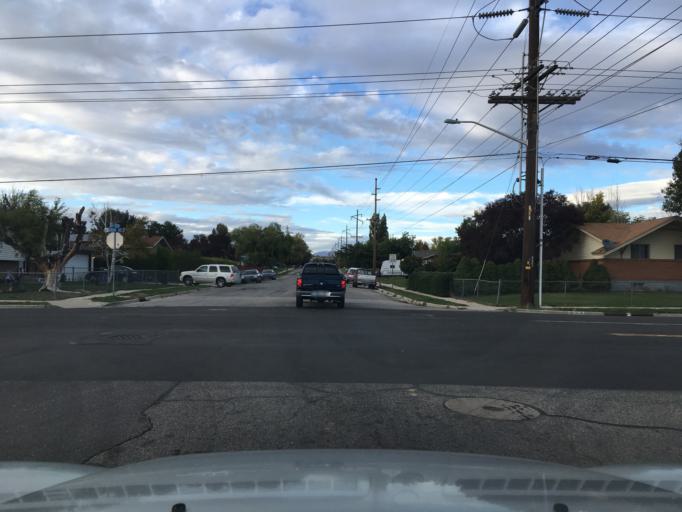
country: US
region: Utah
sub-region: Davis County
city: Layton
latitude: 41.0745
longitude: -111.9879
